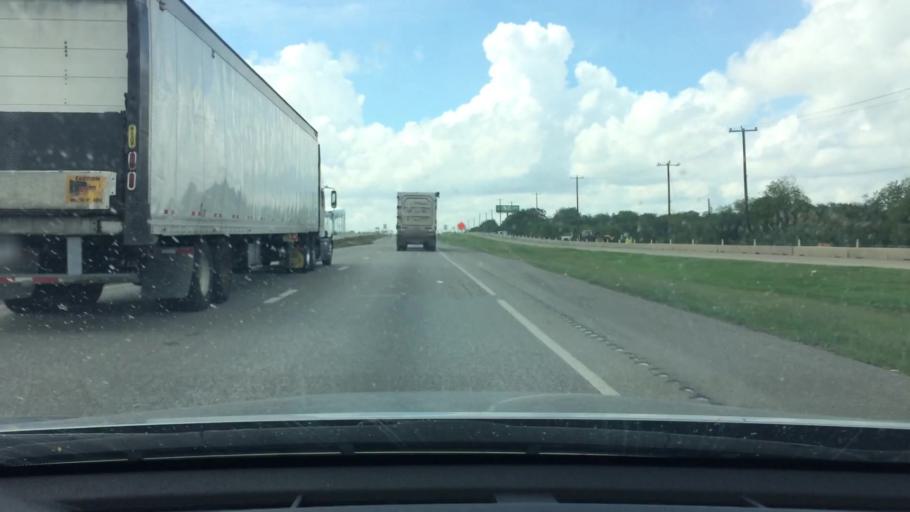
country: US
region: Texas
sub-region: Bexar County
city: Kirby
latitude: 29.4545
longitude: -98.3316
